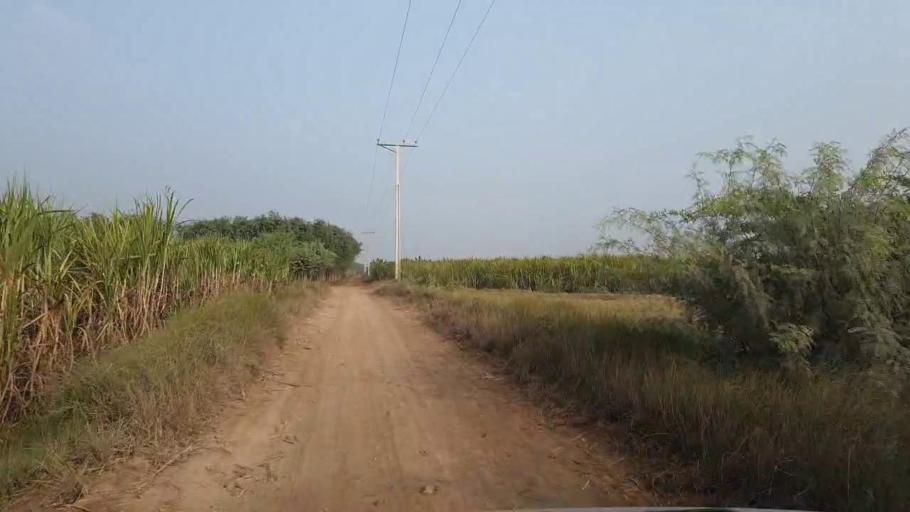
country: PK
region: Sindh
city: Tando Muhammad Khan
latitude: 25.1529
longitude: 68.5871
